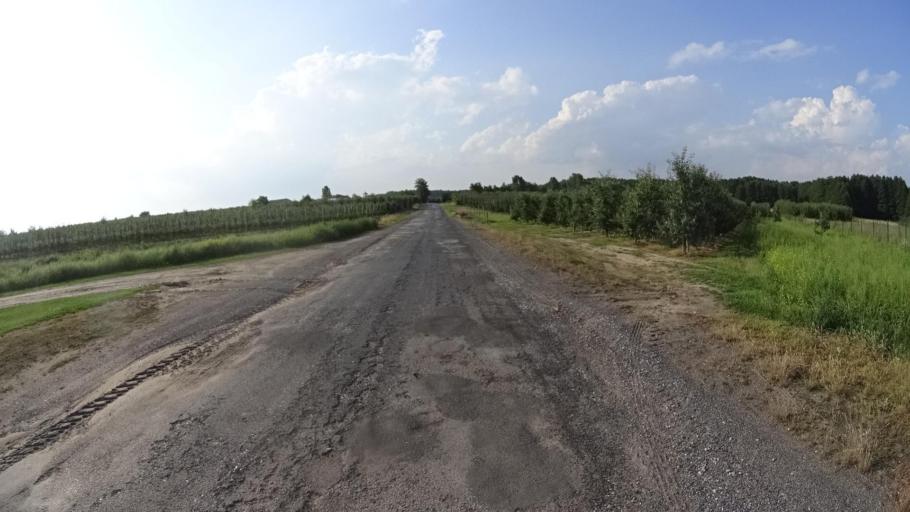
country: PL
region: Masovian Voivodeship
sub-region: Powiat grojecki
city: Goszczyn
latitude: 51.7097
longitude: 20.7918
